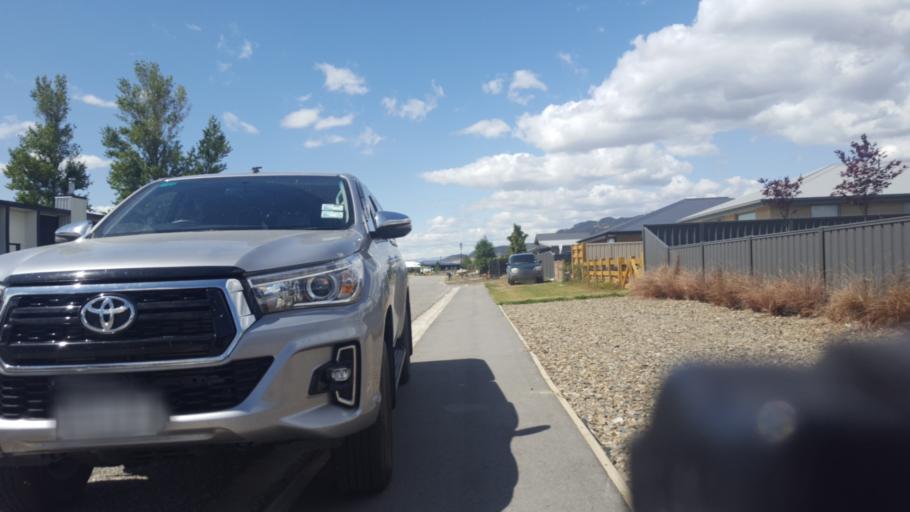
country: NZ
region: Otago
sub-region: Queenstown-Lakes District
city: Wanaka
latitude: -44.9737
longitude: 169.2423
